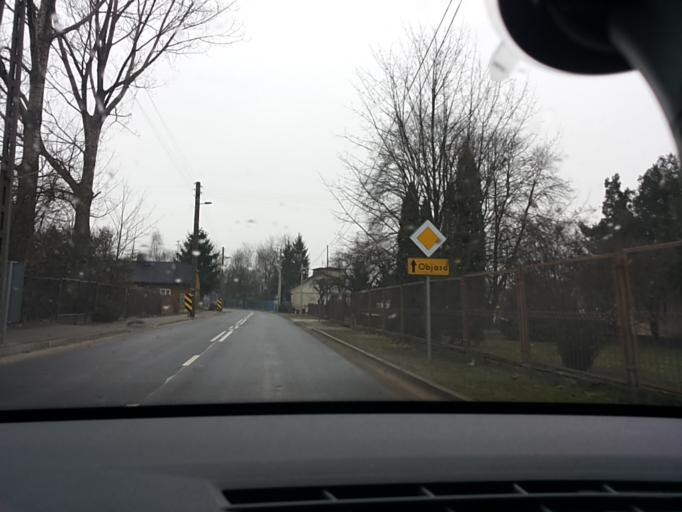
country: PL
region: Lodz Voivodeship
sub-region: Skierniewice
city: Skierniewice
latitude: 51.9668
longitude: 20.1357
